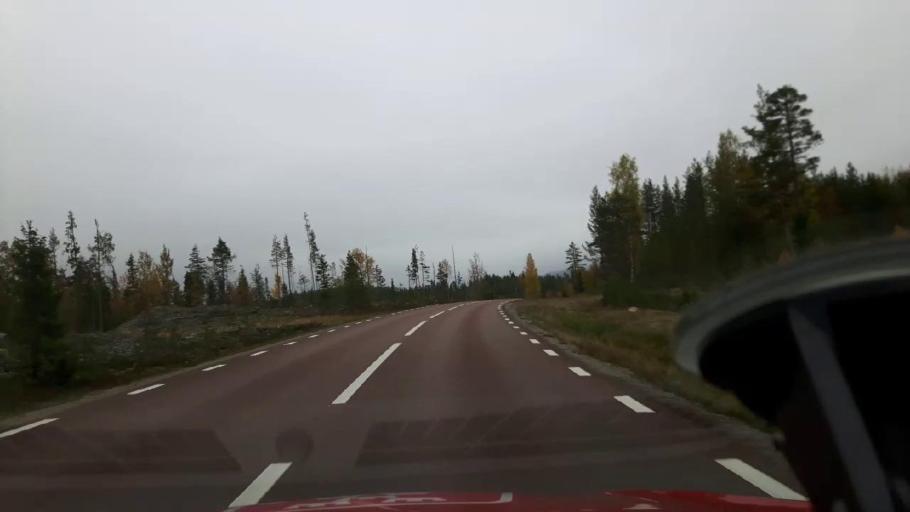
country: SE
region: Jaemtland
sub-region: Bergs Kommun
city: Hoverberg
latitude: 62.4316
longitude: 14.5967
